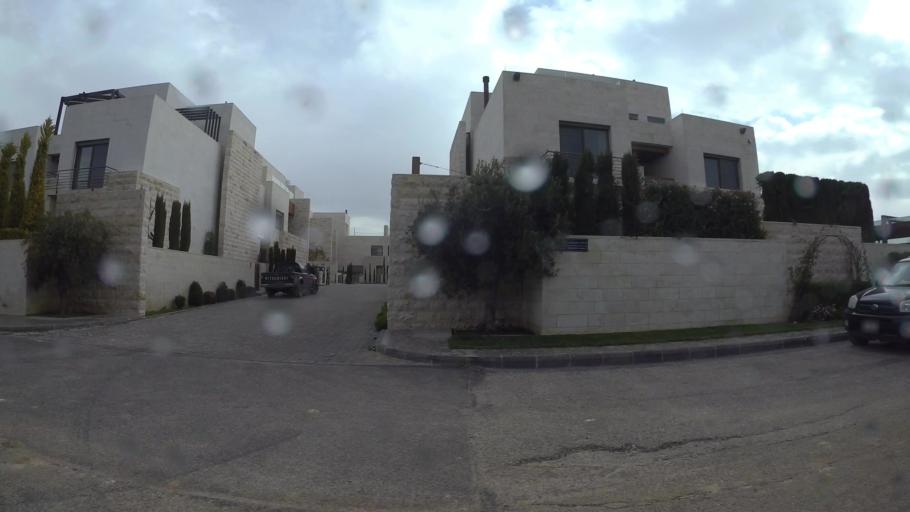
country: JO
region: Amman
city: Wadi as Sir
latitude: 31.9850
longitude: 35.8176
